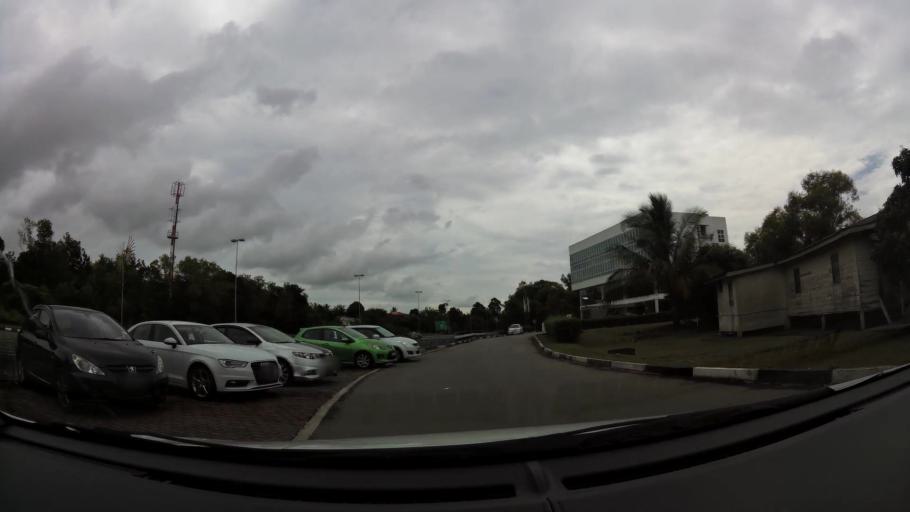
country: BN
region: Brunei and Muara
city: Bandar Seri Begawan
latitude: 4.8976
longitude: 114.9153
